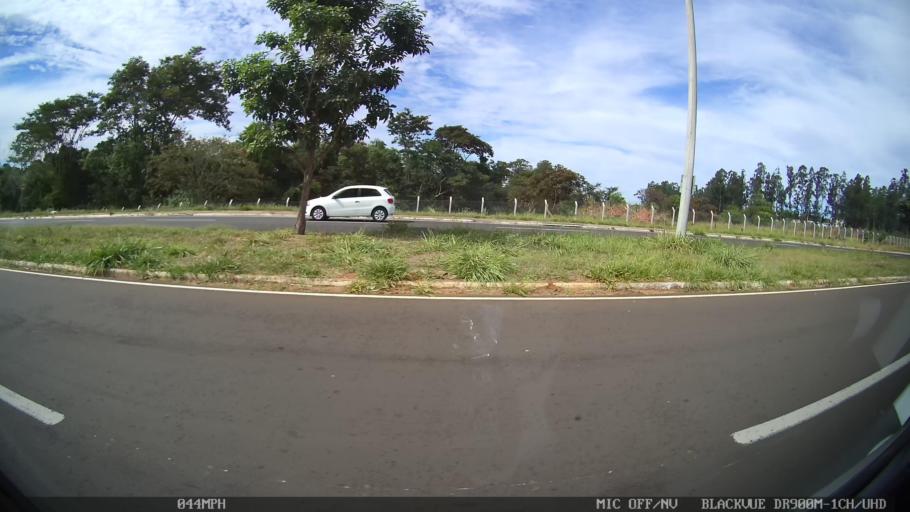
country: BR
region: Sao Paulo
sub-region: Catanduva
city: Catanduva
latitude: -21.1519
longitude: -48.9524
